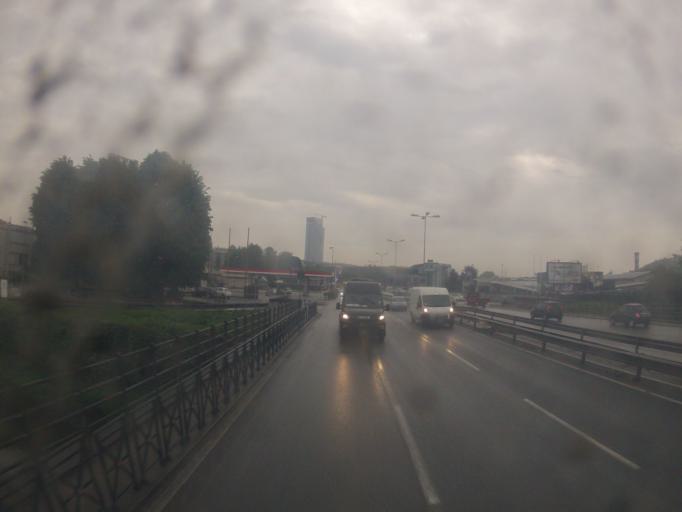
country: IT
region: Piedmont
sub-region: Provincia di Torino
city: Moncalieri
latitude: 45.0133
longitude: 7.6694
